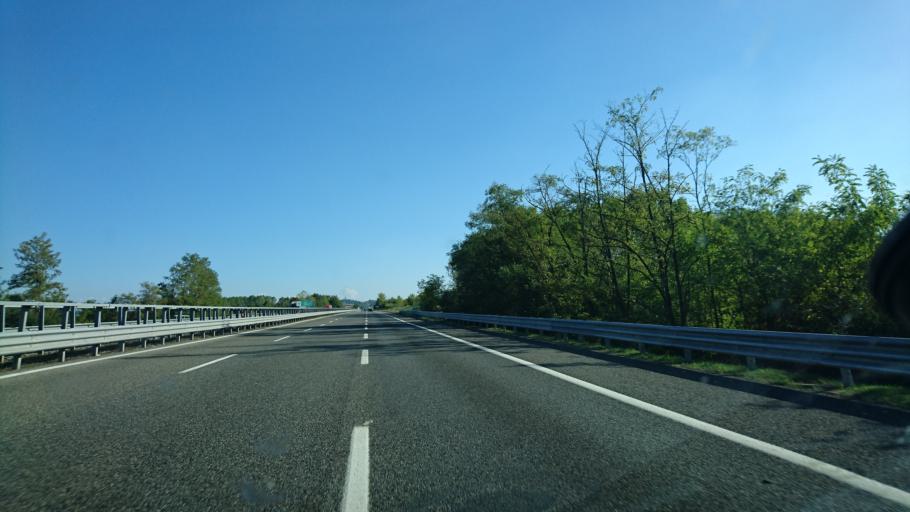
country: IT
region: Piedmont
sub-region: Provincia di Alessandria
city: Mirabello Monferrato
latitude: 45.0381
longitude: 8.5307
